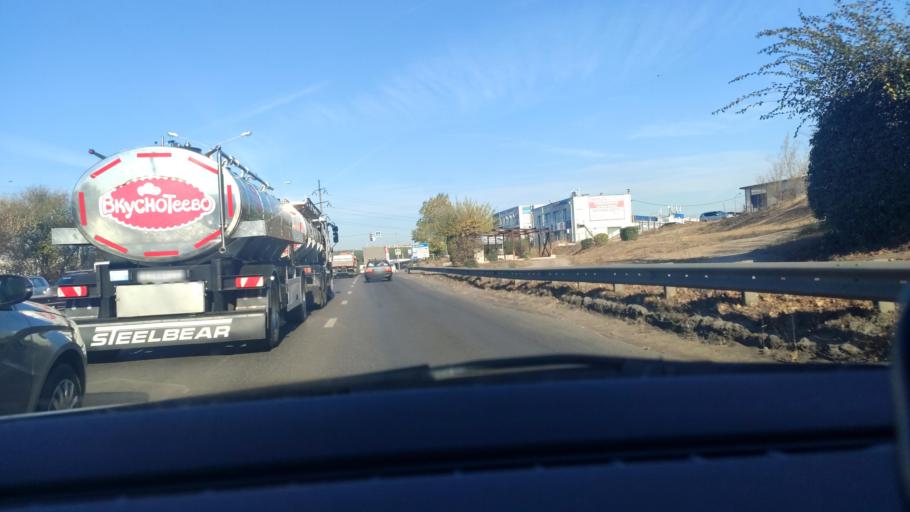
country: RU
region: Voronezj
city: Voronezh
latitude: 51.6655
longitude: 39.1278
